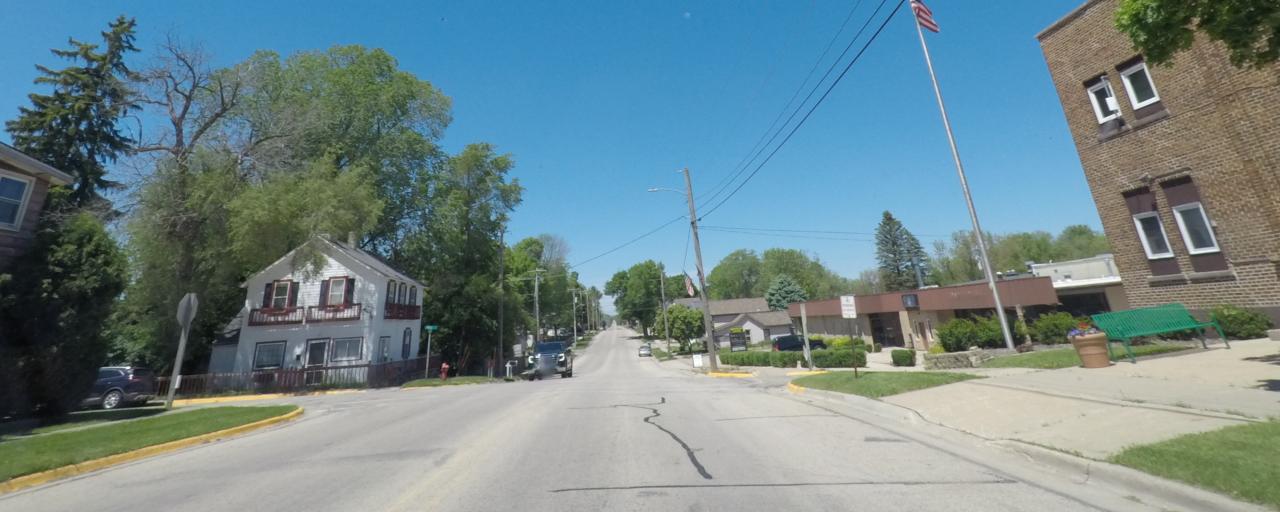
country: US
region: Wisconsin
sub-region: Green County
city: Brooklyn
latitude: 42.8530
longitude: -89.3691
